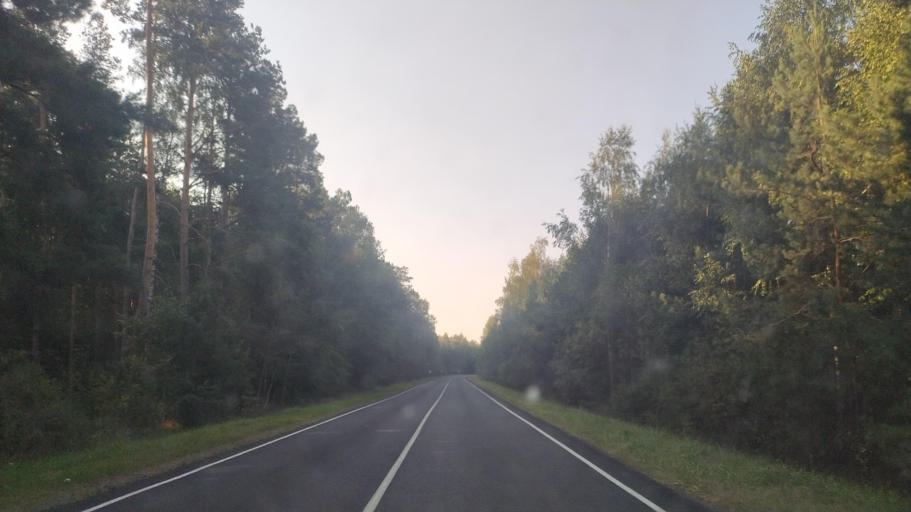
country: BY
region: Brest
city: Drahichyn
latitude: 52.2797
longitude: 25.0710
